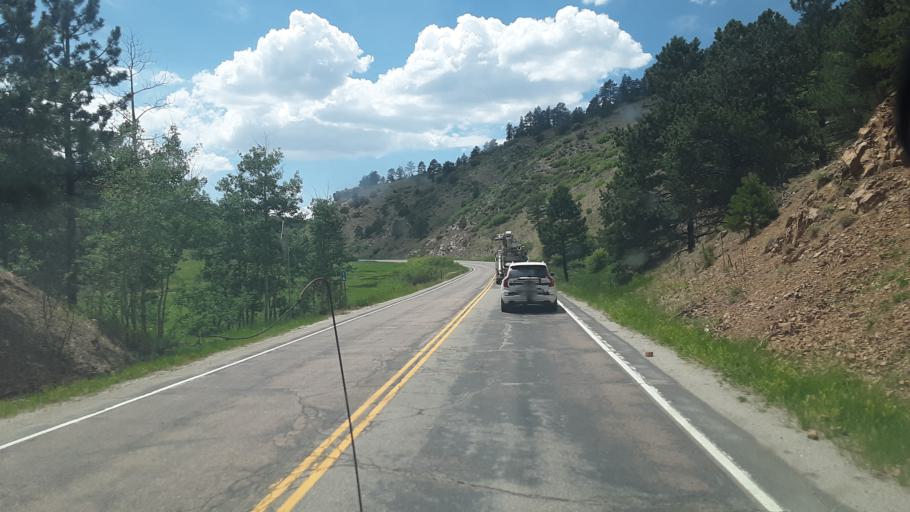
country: US
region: Colorado
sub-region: Fremont County
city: Florence
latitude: 38.1664
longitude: -105.2002
